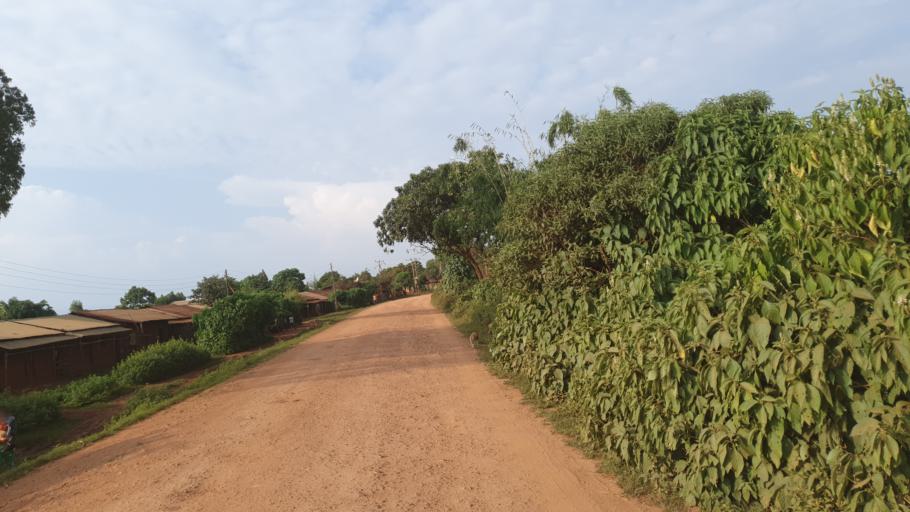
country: ET
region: Oromiya
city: Shambu
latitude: 9.4714
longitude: 36.5335
